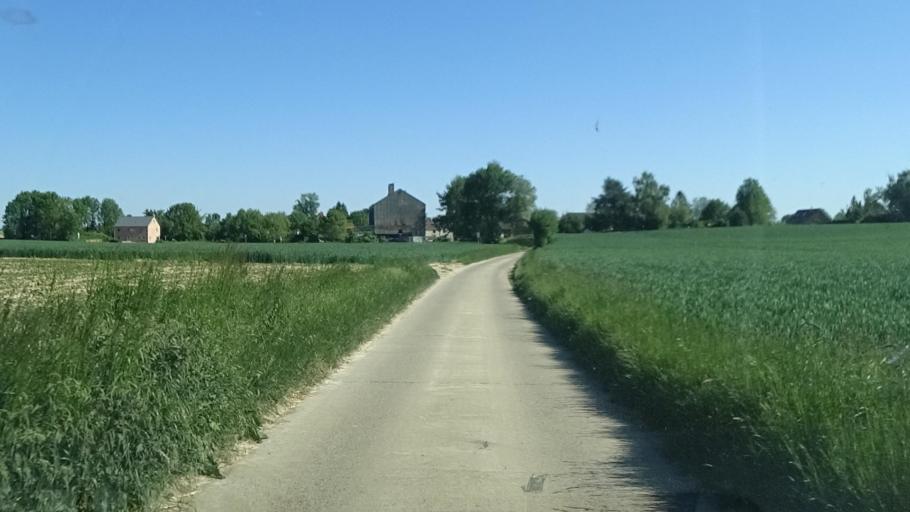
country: BE
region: Wallonia
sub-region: Province du Brabant Wallon
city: Walhain-Saint-Paul
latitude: 50.6495
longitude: 4.6855
